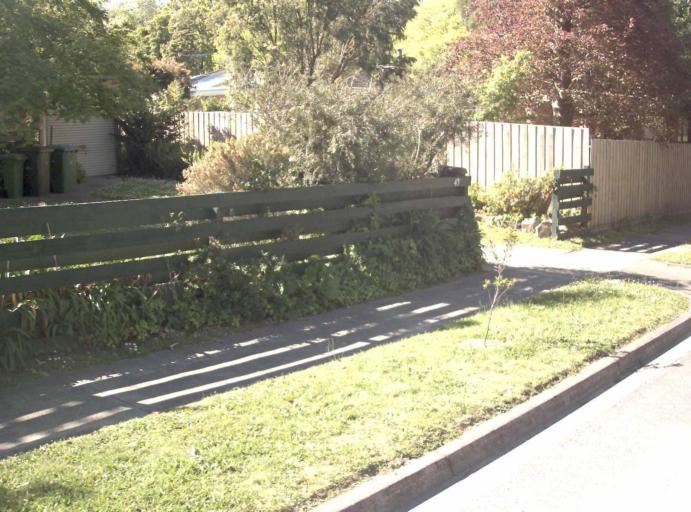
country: AU
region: Victoria
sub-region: Maroondah
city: Croydon South
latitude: -37.7977
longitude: 145.2762
